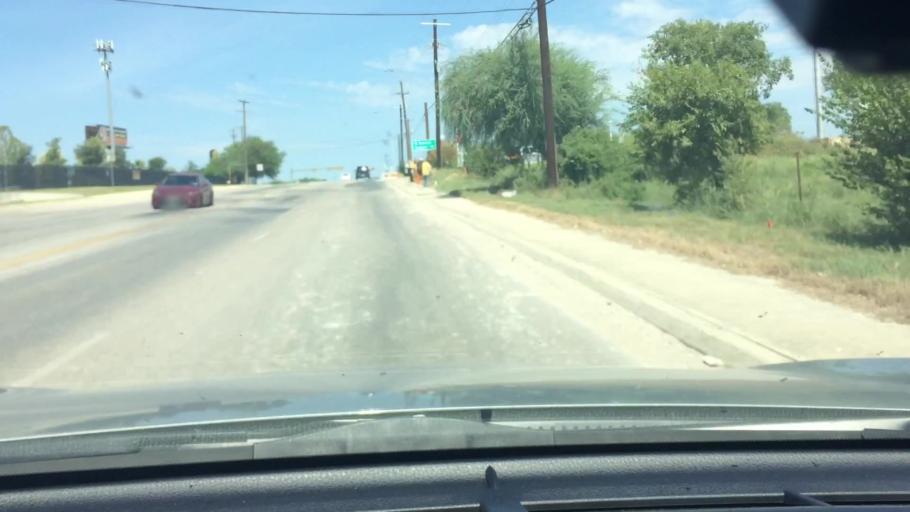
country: US
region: Texas
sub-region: Bexar County
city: San Antonio
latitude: 29.4013
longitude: -98.4414
